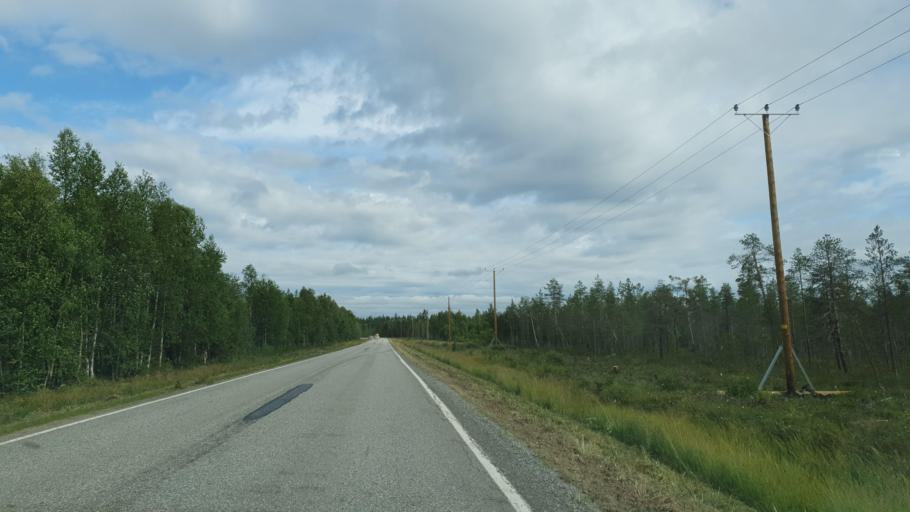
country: FI
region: Lapland
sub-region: Pohjois-Lappi
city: Sodankylae
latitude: 67.4866
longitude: 26.0944
